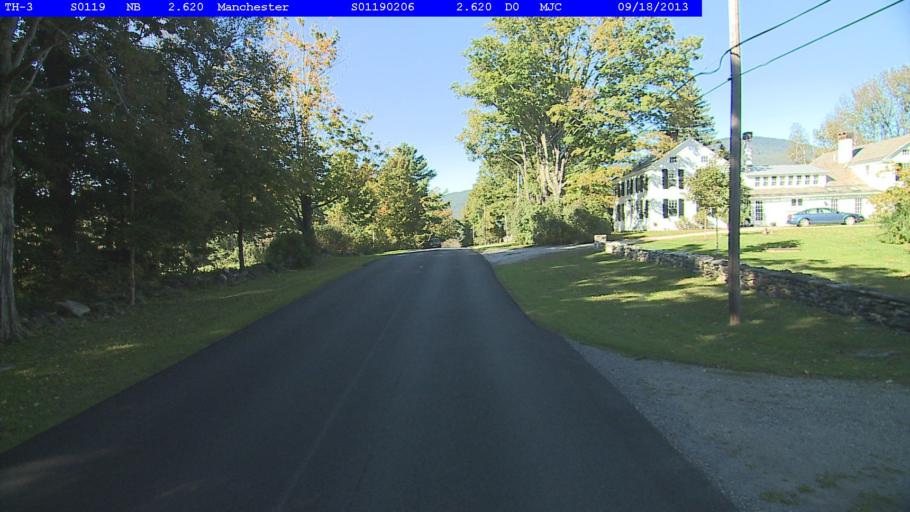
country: US
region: Vermont
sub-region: Bennington County
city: Manchester Center
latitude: 43.2009
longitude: -73.0693
